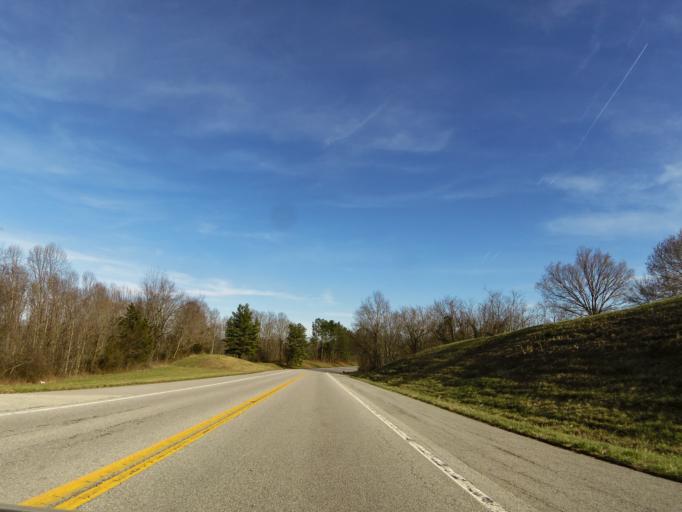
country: US
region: Tennessee
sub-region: Cannon County
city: Woodbury
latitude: 35.8065
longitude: -86.0244
